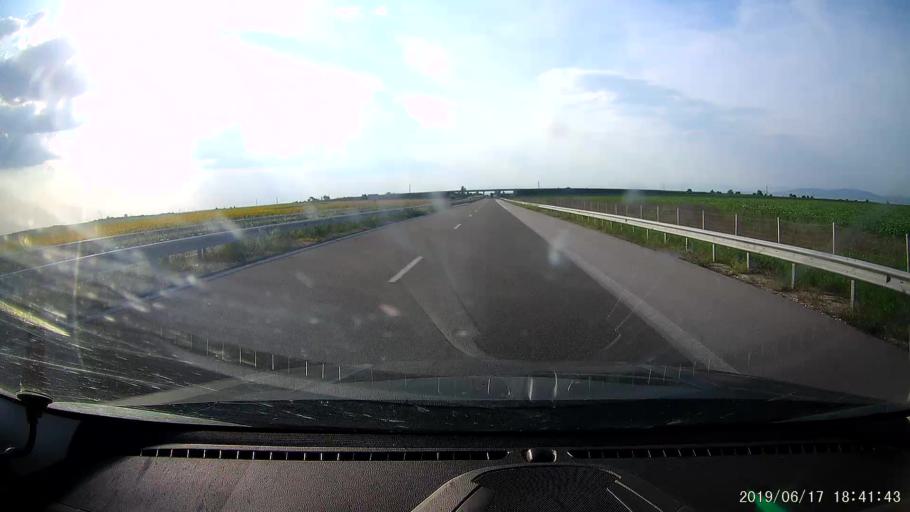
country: BG
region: Stara Zagora
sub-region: Obshtina Chirpan
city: Chirpan
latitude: 42.1776
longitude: 25.2506
